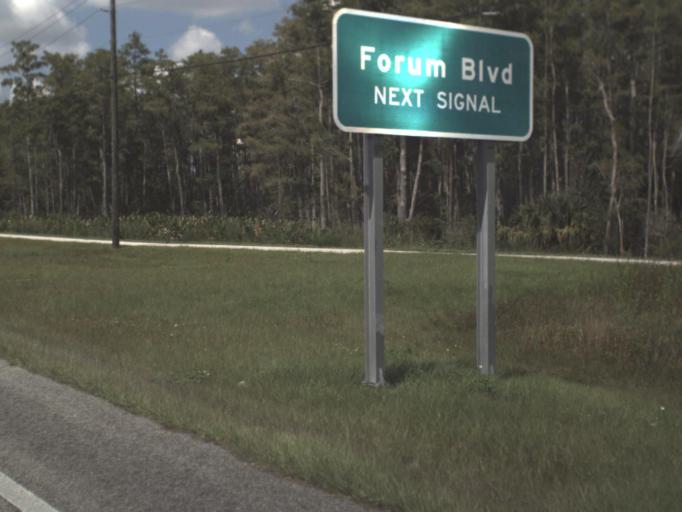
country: US
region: Florida
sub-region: Lee County
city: Fort Myers
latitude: 26.6131
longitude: -81.7941
